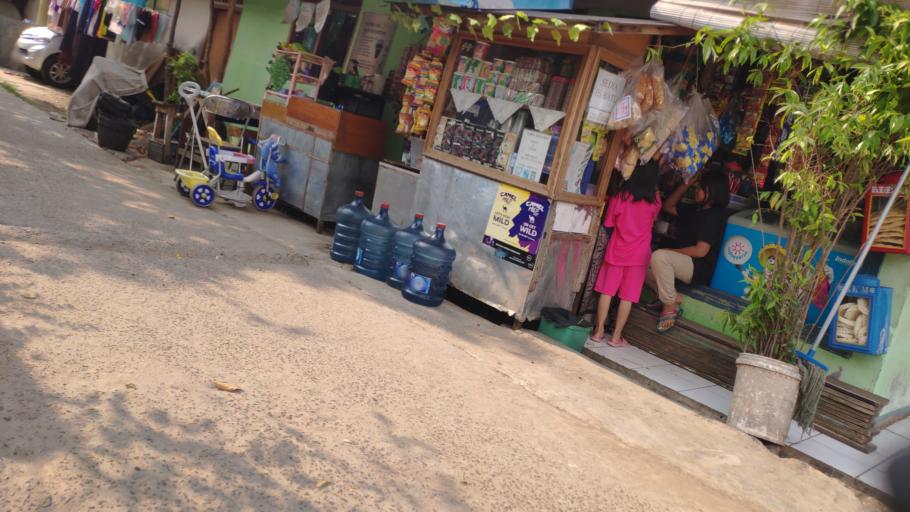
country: ID
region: West Java
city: Pamulang
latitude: -6.3294
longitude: 106.7953
